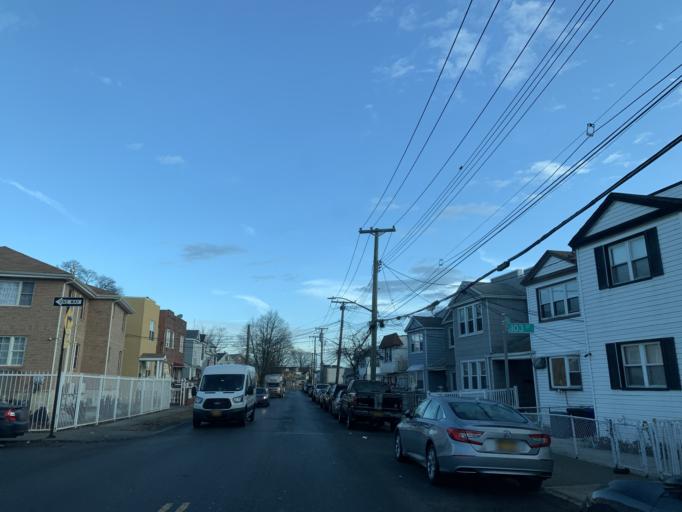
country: US
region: New York
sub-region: Queens County
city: Borough of Queens
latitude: 40.6772
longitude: -73.8351
